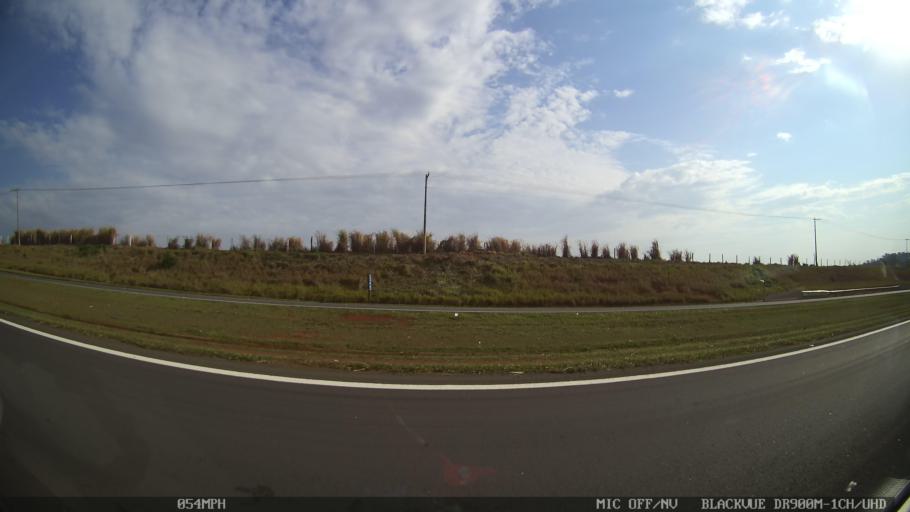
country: BR
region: Sao Paulo
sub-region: Paulinia
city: Paulinia
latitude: -22.7012
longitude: -47.1468
